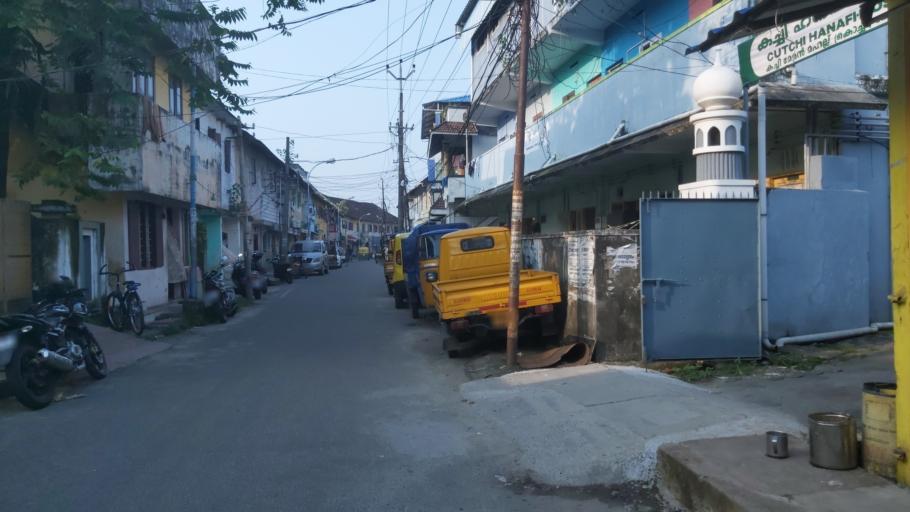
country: IN
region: Kerala
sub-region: Ernakulam
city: Cochin
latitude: 9.9633
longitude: 76.2548
